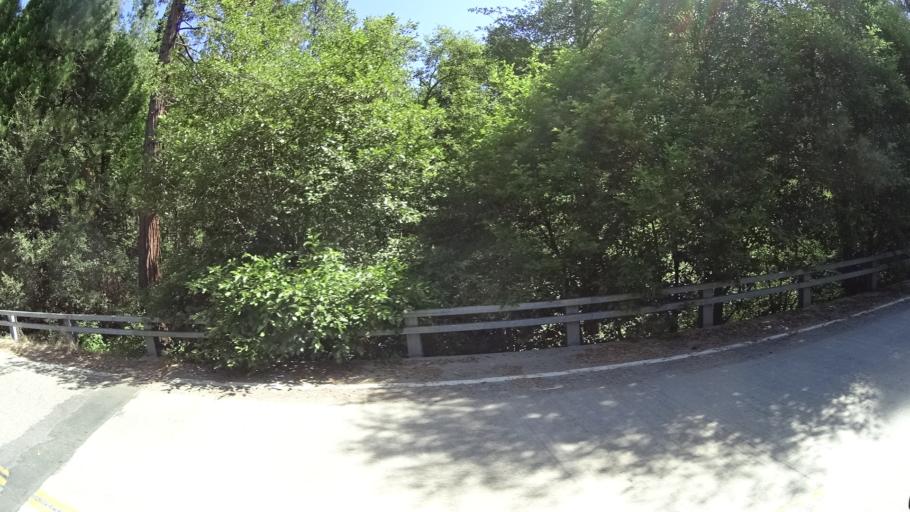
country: US
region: California
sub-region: Amador County
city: Pioneer
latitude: 38.3668
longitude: -120.5024
